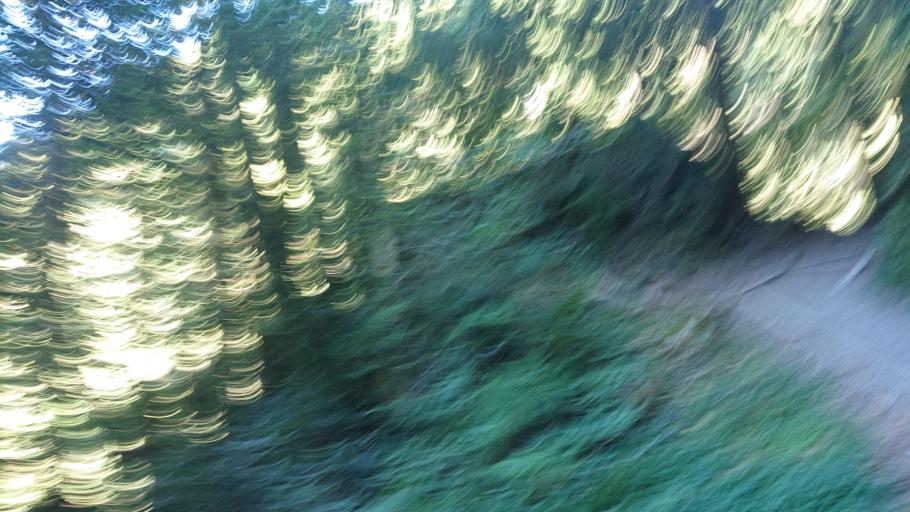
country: TW
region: Taiwan
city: Lugu
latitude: 23.4798
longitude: 120.8239
